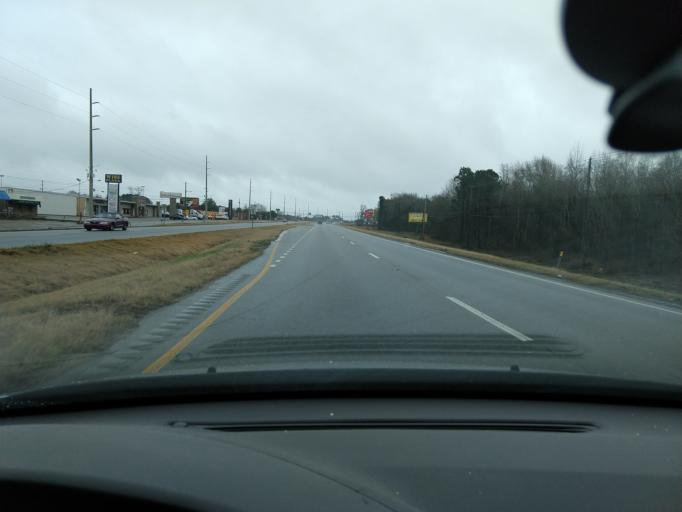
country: US
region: Alabama
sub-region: Houston County
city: Dothan
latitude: 31.2533
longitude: -85.3971
